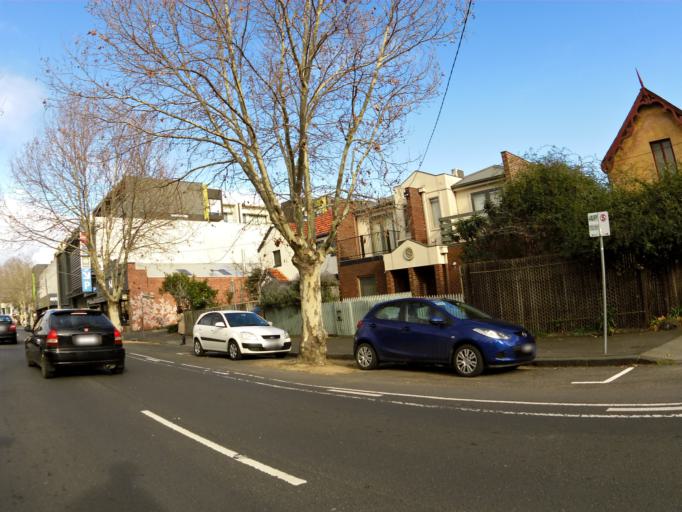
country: AU
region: Victoria
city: Abbotsford
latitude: -37.8083
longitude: 144.9962
